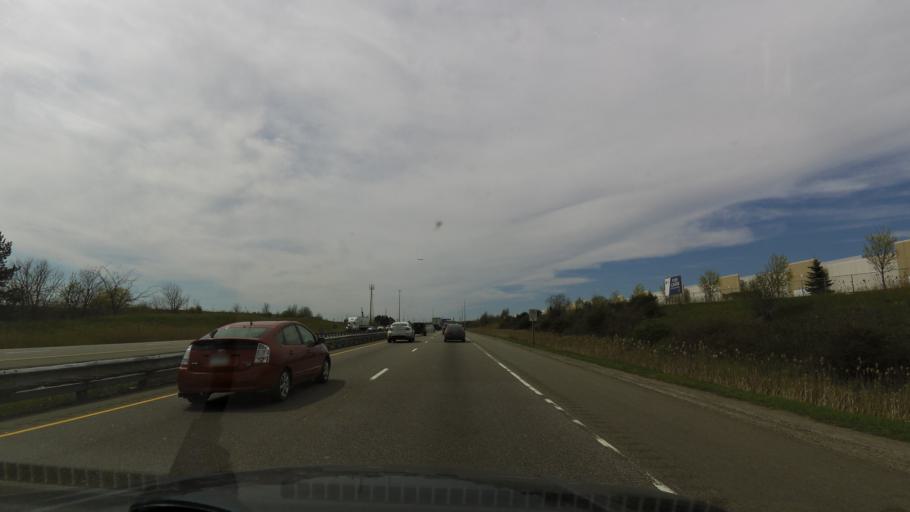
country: CA
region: Ontario
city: Oakville
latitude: 43.5201
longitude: -79.7091
